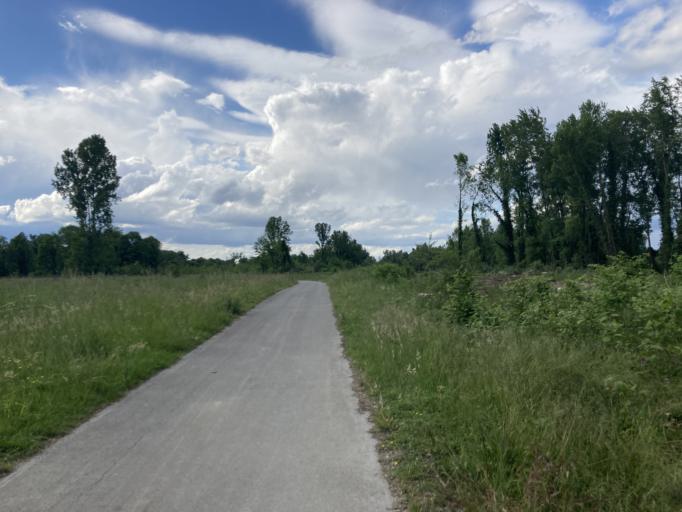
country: FR
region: Aquitaine
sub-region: Departement des Pyrenees-Atlantiques
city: Arbus
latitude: 43.3444
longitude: -0.5056
